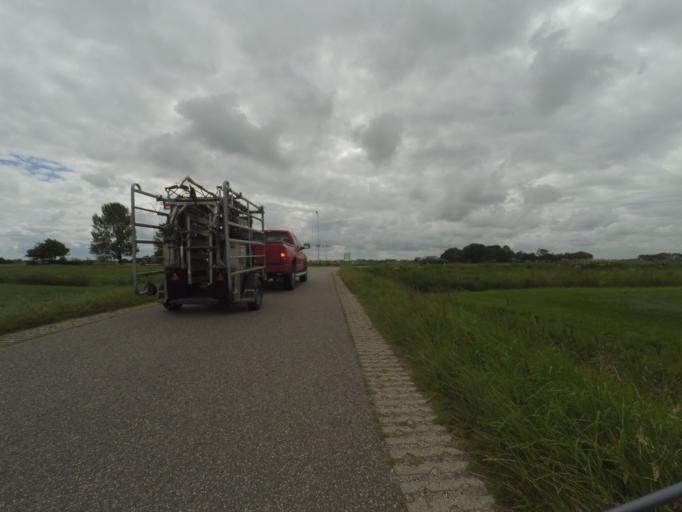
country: NL
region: Friesland
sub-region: Gemeente Dongeradeel
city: Anjum
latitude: 53.3207
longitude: 6.1009
